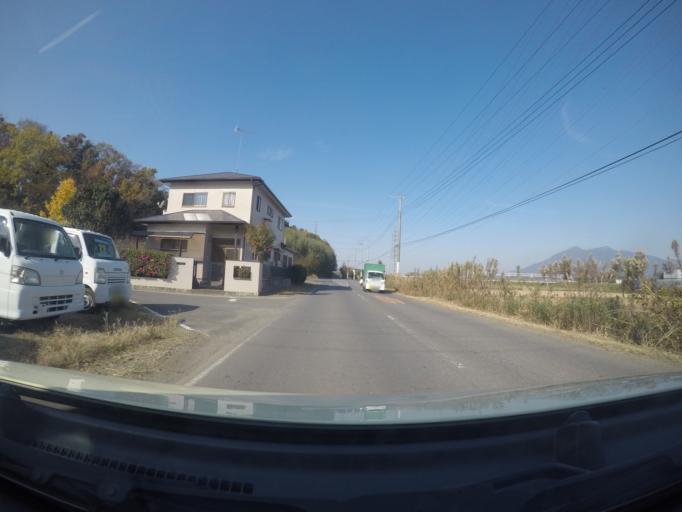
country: JP
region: Ibaraki
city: Tsukuba
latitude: 36.1587
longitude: 140.0848
